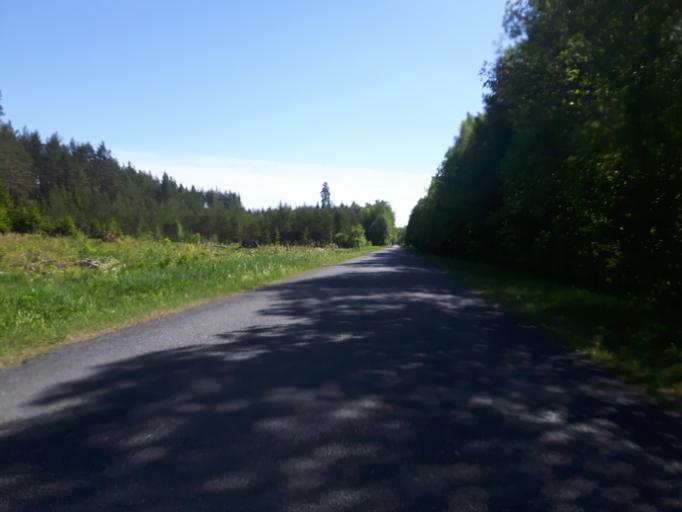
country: EE
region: Laeaene-Virumaa
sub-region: Haljala vald
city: Haljala
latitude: 59.5487
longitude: 26.2379
